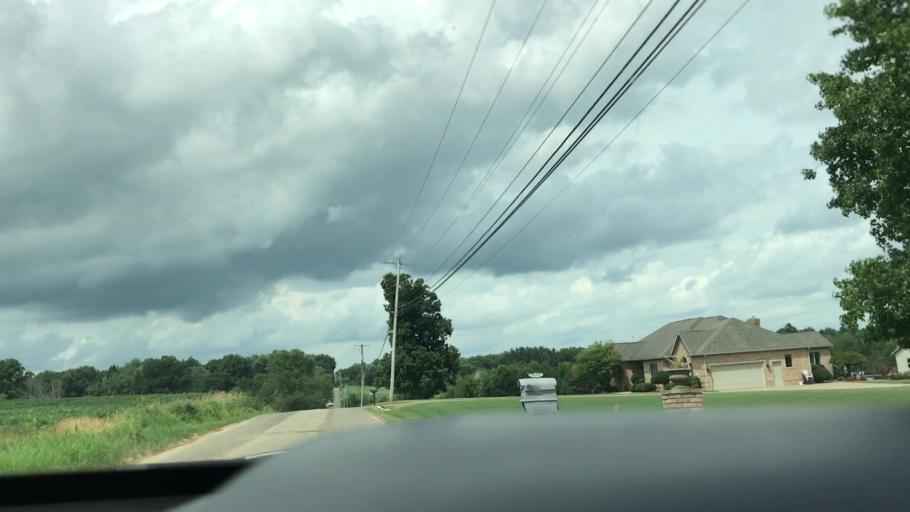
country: US
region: Ohio
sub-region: Stark County
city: Massillon
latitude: 40.7785
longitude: -81.5645
